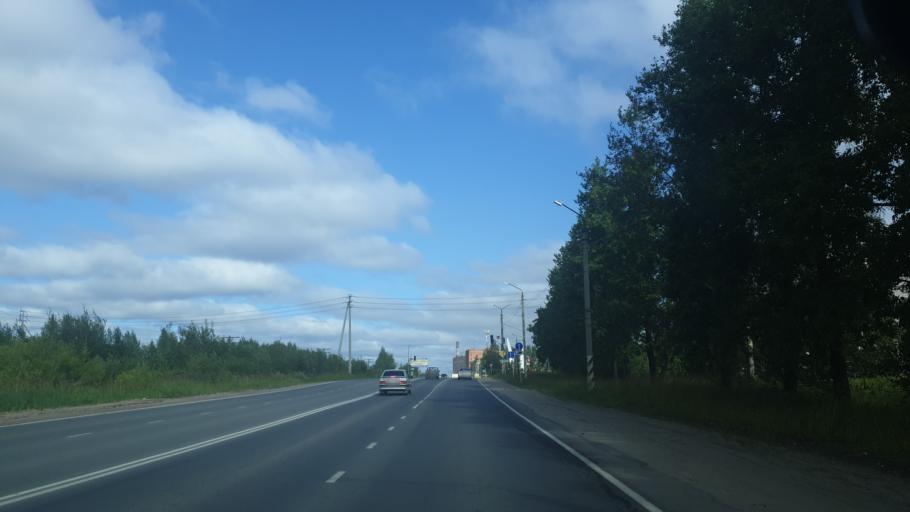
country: RU
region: Komi Republic
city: Ezhva
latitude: 61.7943
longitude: 50.7394
